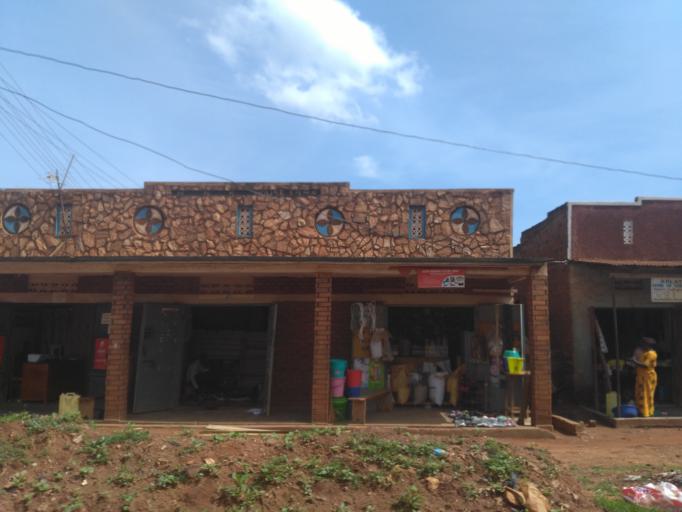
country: UG
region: Central Region
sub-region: Wakiso District
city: Kireka
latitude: 0.4393
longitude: 32.6006
